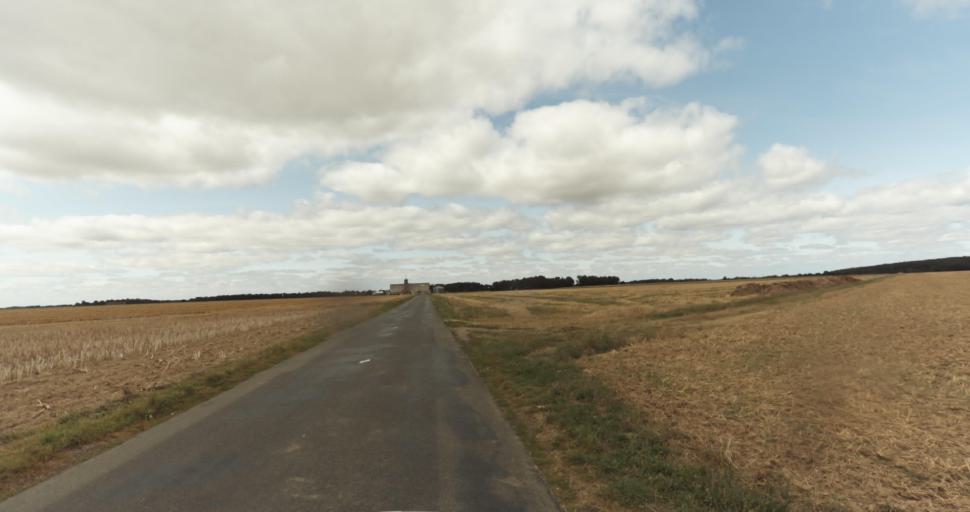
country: FR
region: Haute-Normandie
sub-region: Departement de l'Eure
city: Arnieres-sur-Iton
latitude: 48.9232
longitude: 1.1710
